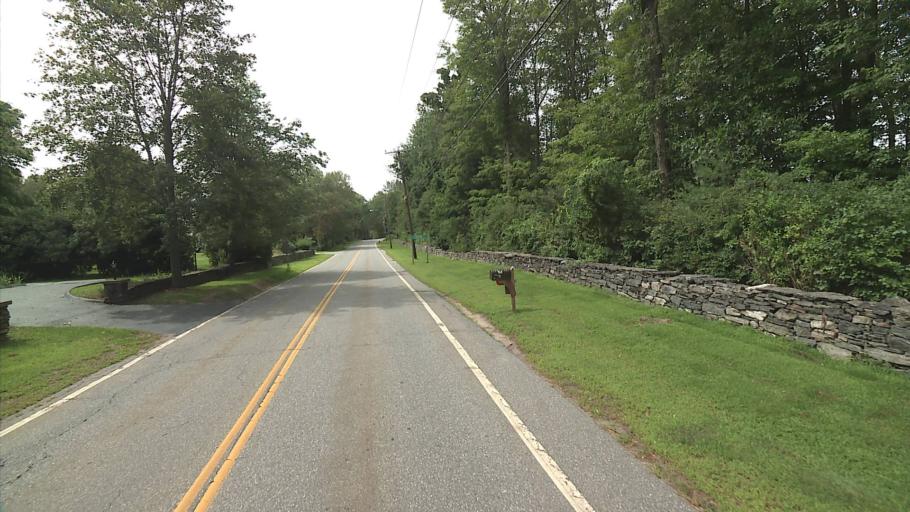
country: US
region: Connecticut
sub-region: Windham County
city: Thompson
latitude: 41.9527
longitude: -71.8673
